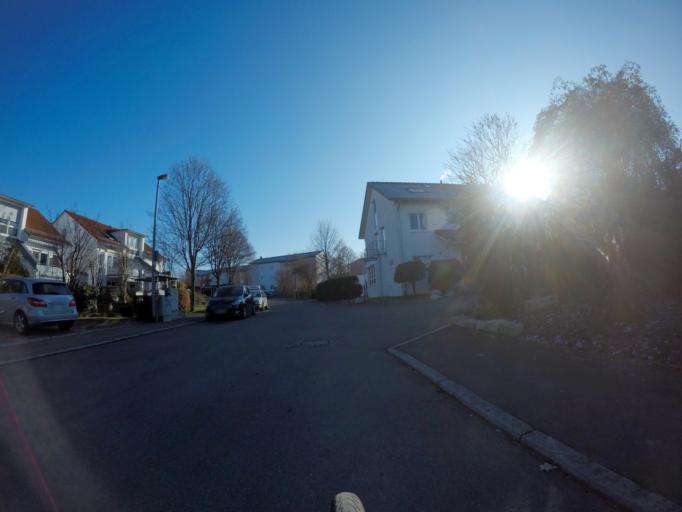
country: DE
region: Baden-Wuerttemberg
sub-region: Tuebingen Region
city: Reutlingen
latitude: 48.5206
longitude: 9.2208
